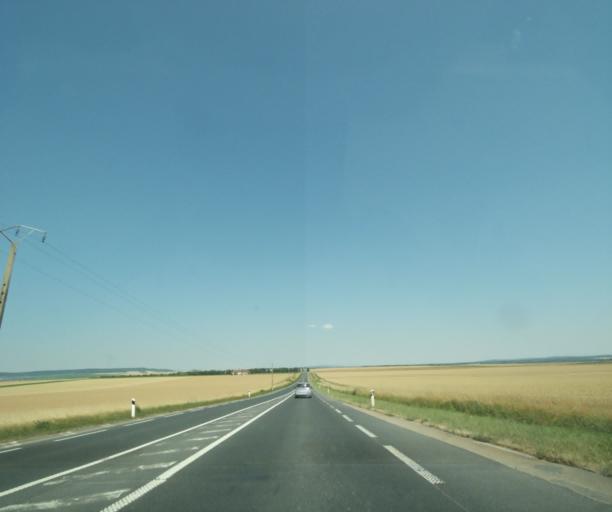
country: FR
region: Champagne-Ardenne
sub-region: Departement de la Marne
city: Mourmelon-le-Grand
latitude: 49.0775
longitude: 4.2852
